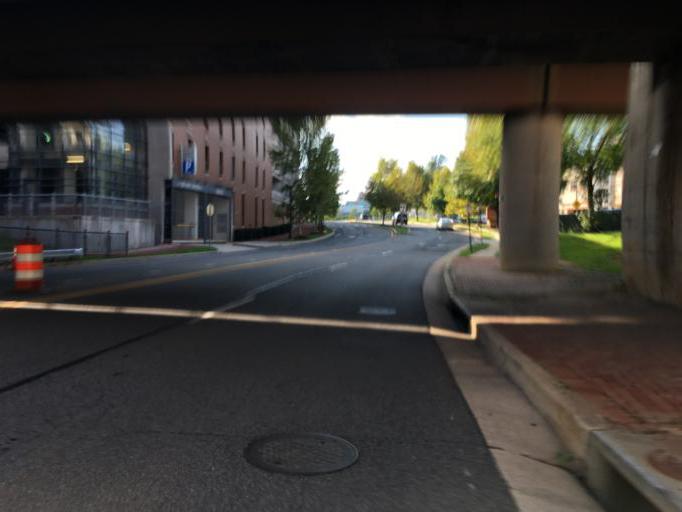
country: US
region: Virginia
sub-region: Fairfax County
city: Huntington
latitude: 38.8025
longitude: -77.0682
